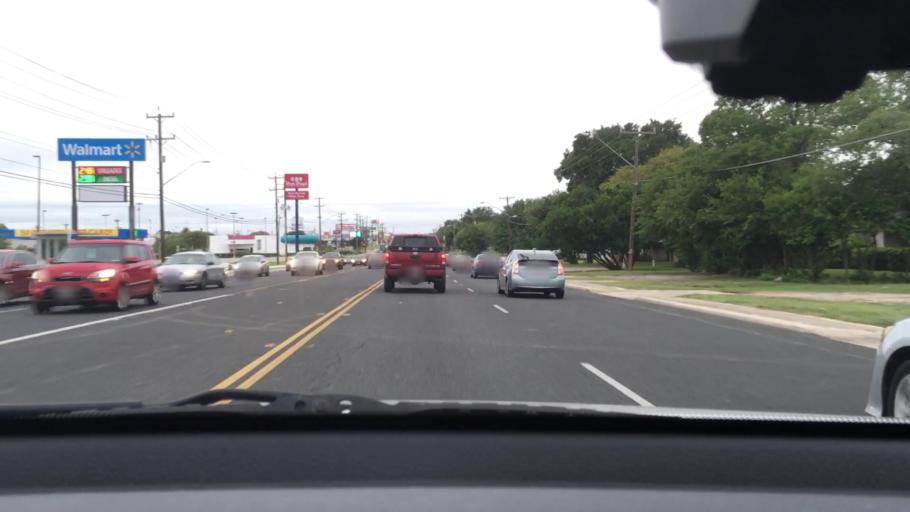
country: US
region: Texas
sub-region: Bexar County
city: Windcrest
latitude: 29.5103
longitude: -98.3738
